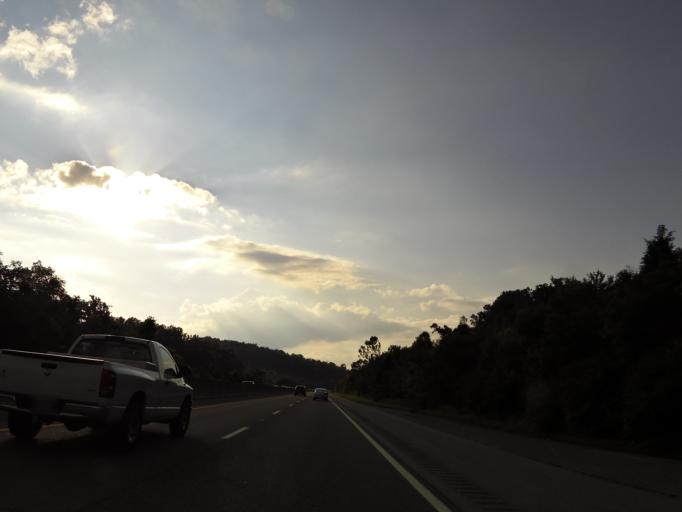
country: US
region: Tennessee
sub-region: Knox County
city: Farragut
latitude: 35.8887
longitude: -84.1081
